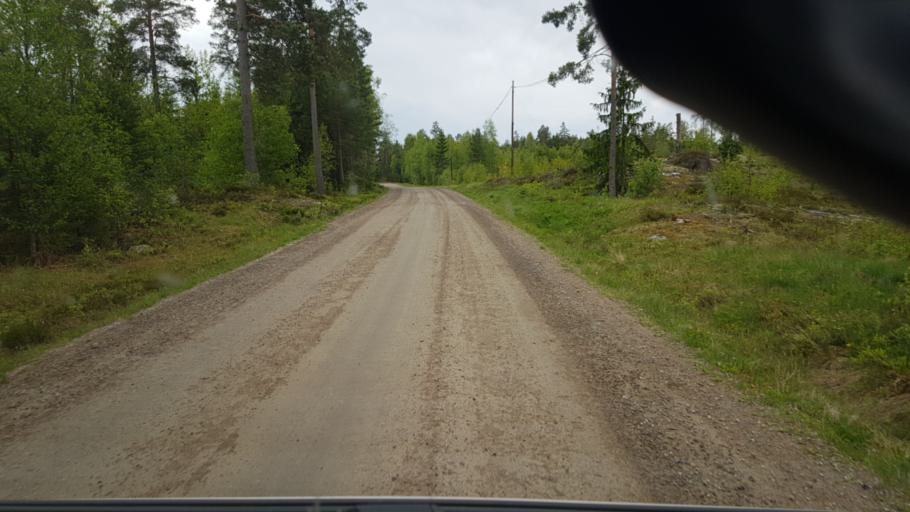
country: SE
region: Vaermland
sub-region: Arvika Kommun
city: Arvika
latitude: 59.5259
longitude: 12.7365
